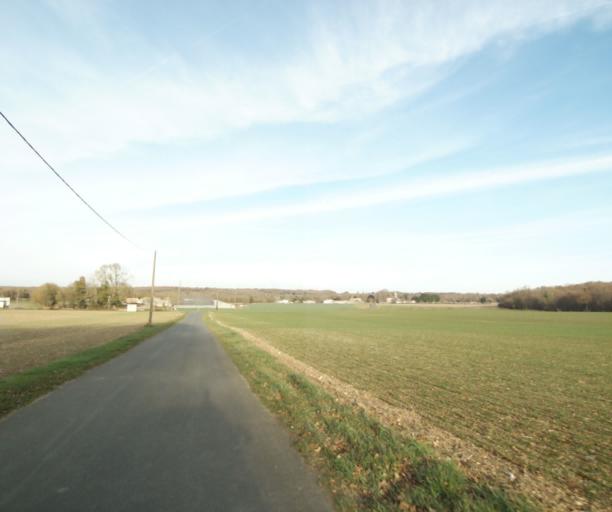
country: FR
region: Poitou-Charentes
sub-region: Departement de la Charente-Maritime
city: Fontcouverte
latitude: 45.8160
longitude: -0.5755
